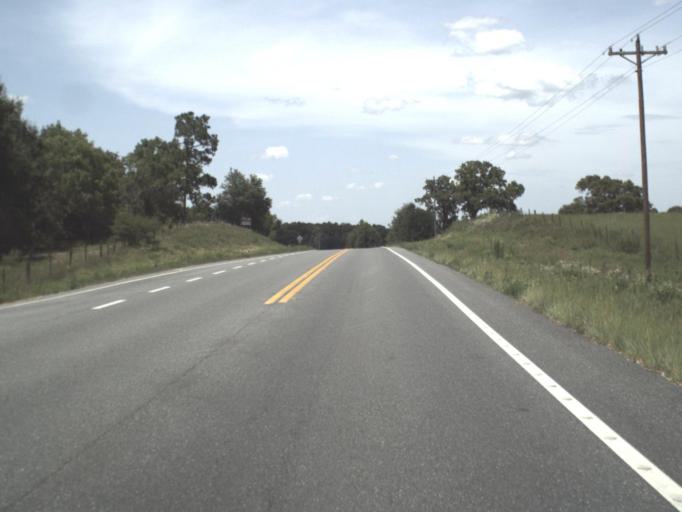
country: US
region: Florida
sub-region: Gilchrist County
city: Trenton
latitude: 29.8618
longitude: -82.8603
